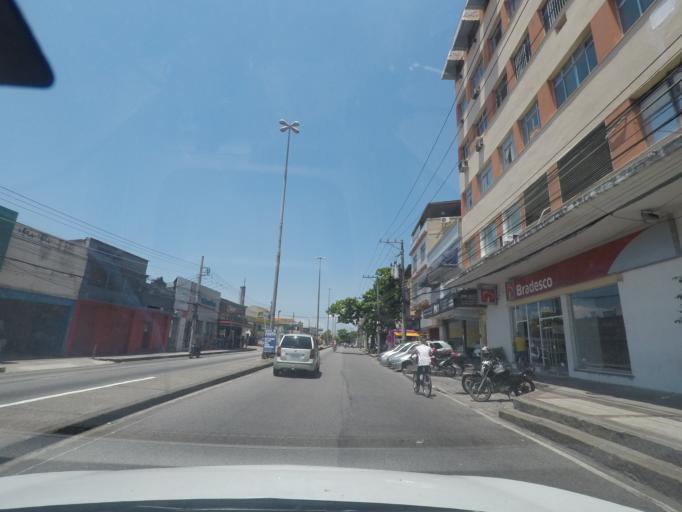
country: BR
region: Rio de Janeiro
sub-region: Rio De Janeiro
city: Rio de Janeiro
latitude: -22.8848
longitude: -43.2982
